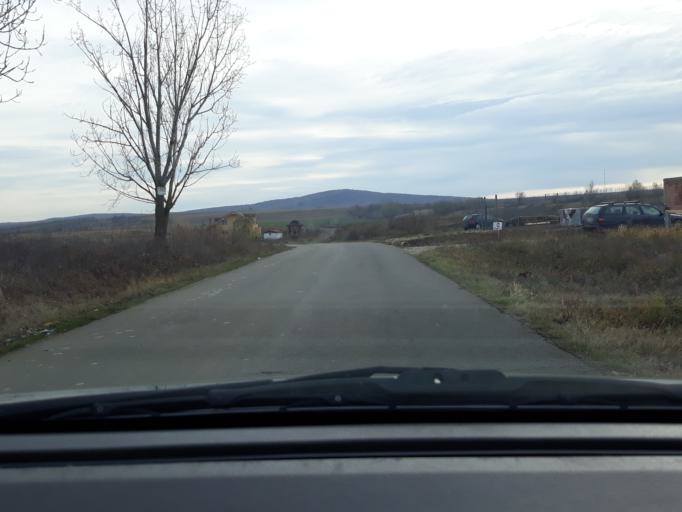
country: RO
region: Bihor
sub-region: Comuna Sanmartin
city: Sanmartin
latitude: 47.0203
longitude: 22.0058
